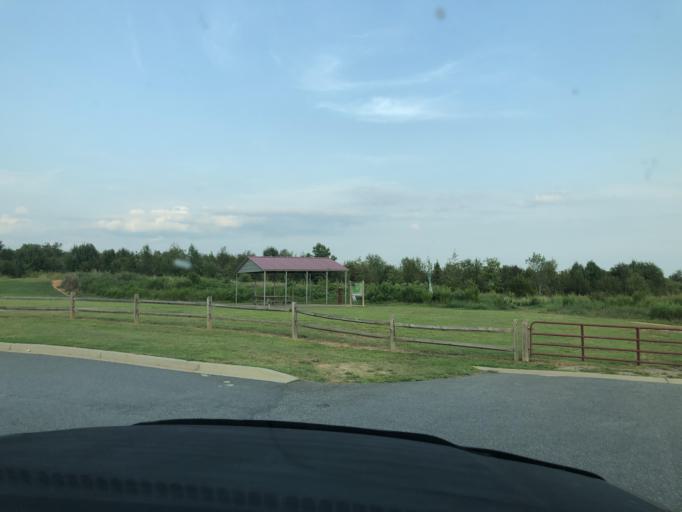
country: US
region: South Carolina
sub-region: Spartanburg County
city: Inman Mills
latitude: 35.0597
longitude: -82.1686
